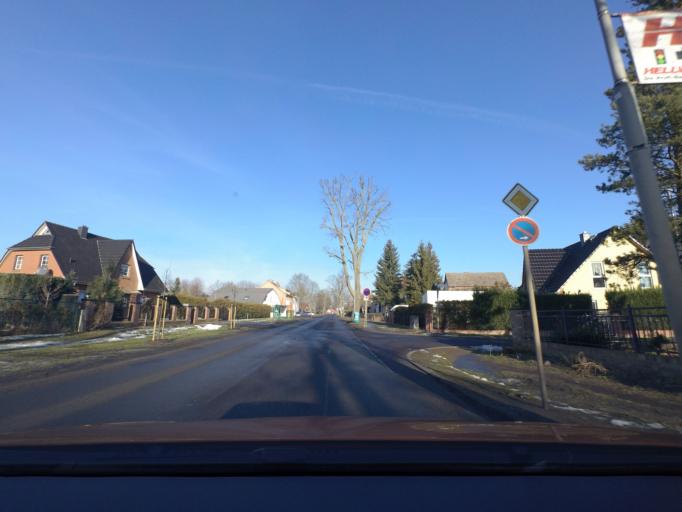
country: DE
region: Brandenburg
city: Falkensee
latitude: 52.5492
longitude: 13.0883
